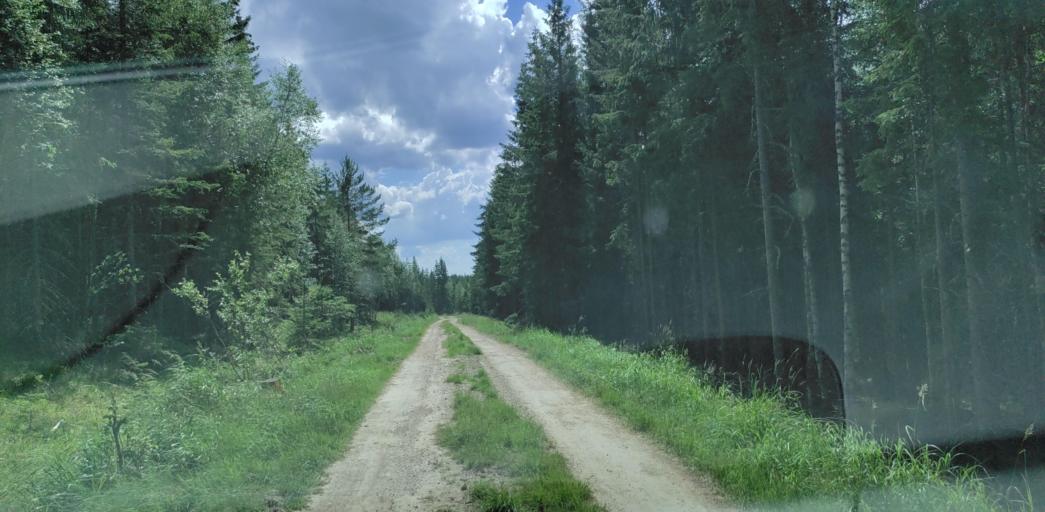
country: SE
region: Vaermland
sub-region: Hagfors Kommun
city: Ekshaerad
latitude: 60.0643
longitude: 13.3395
